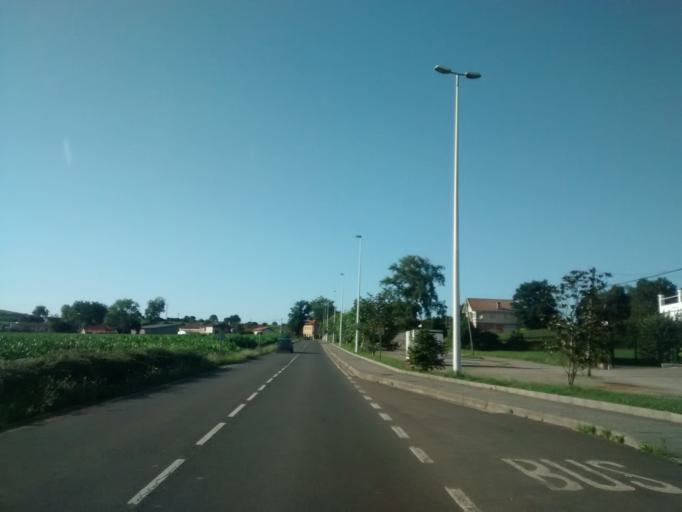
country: ES
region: Cantabria
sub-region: Provincia de Cantabria
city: Lierganes
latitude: 43.4010
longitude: -3.7368
